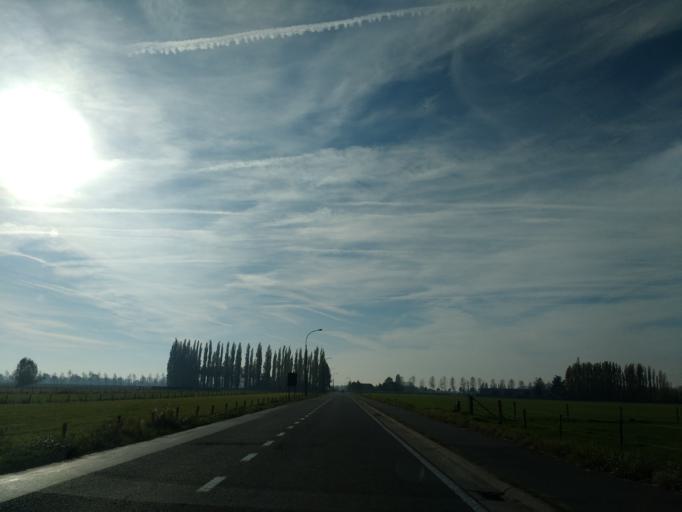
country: BE
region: Flanders
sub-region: Provincie Oost-Vlaanderen
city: Kaprijke
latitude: 51.2671
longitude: 3.6182
